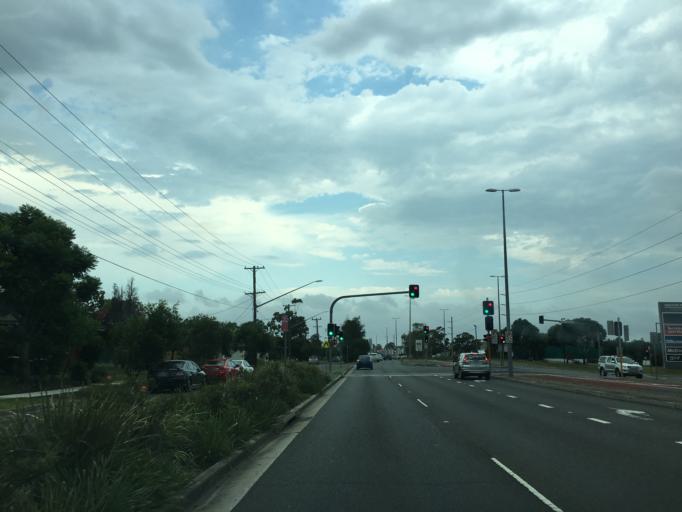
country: AU
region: New South Wales
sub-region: Liverpool
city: Miller
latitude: -33.9274
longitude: 150.8873
